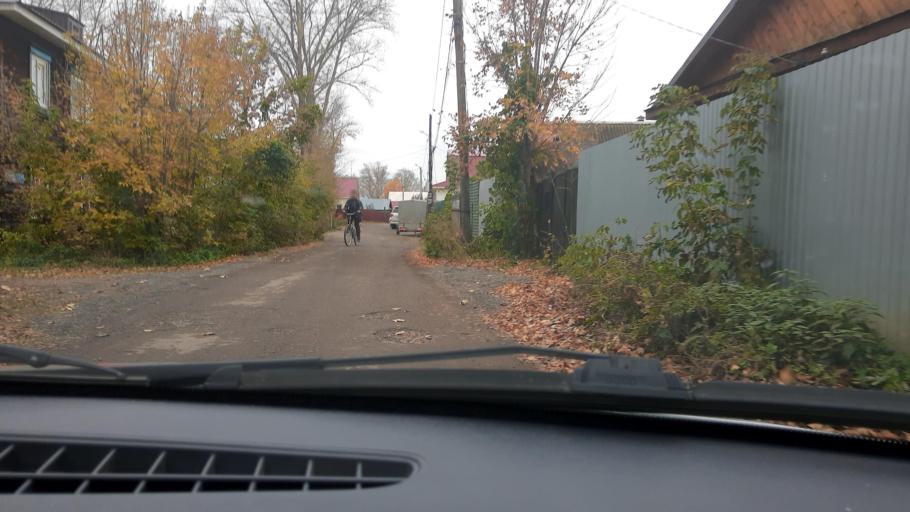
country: RU
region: Bashkortostan
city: Mikhaylovka
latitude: 54.7870
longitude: 55.8798
